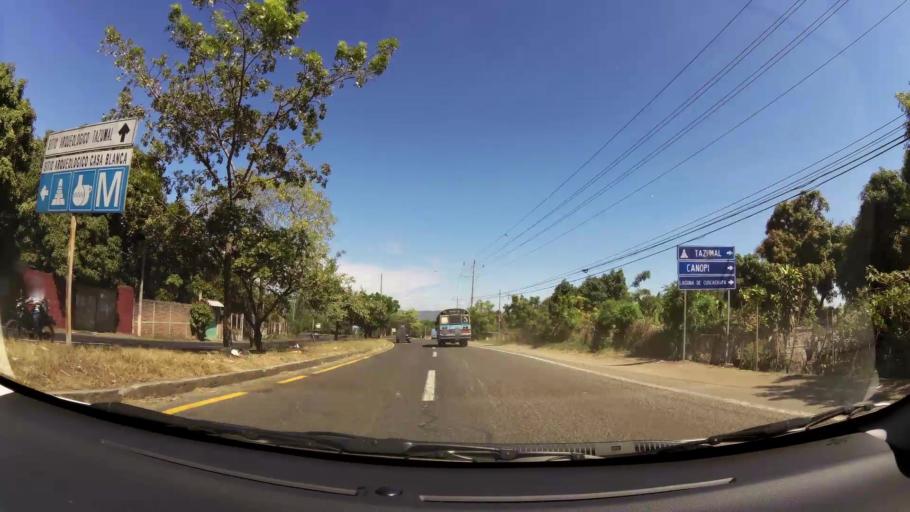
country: SV
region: Santa Ana
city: Chalchuapa
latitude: 13.9762
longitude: -89.6918
